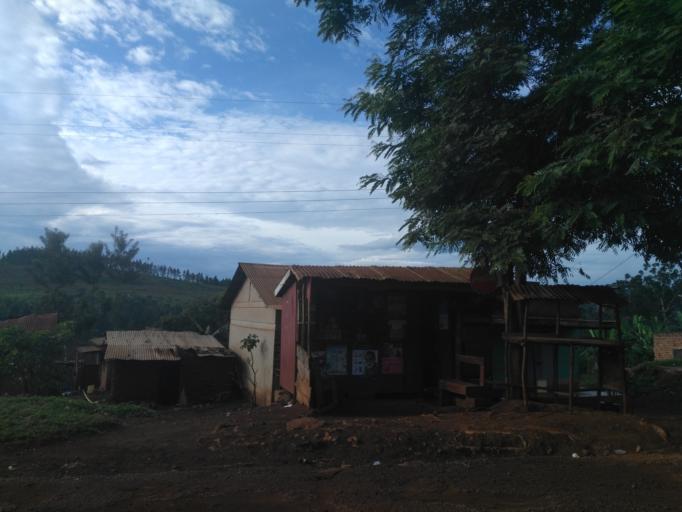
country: UG
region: Eastern Region
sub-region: Jinja District
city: Jinja
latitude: 0.4649
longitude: 33.1793
